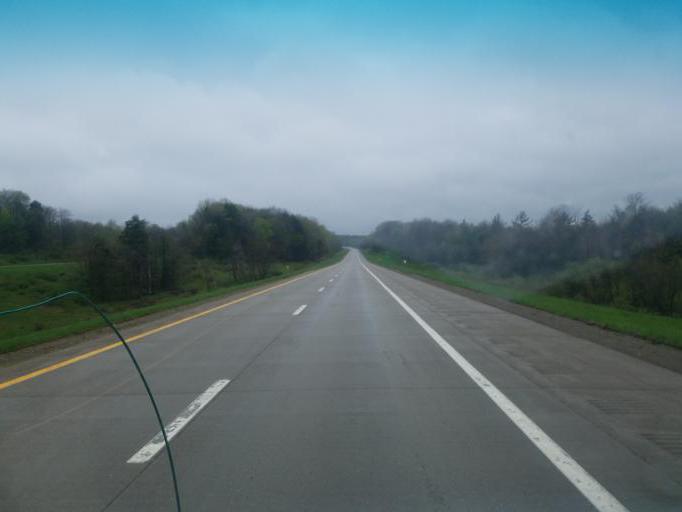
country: US
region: New York
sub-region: Chautauqua County
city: Clymer
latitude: 42.1438
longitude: -79.6876
